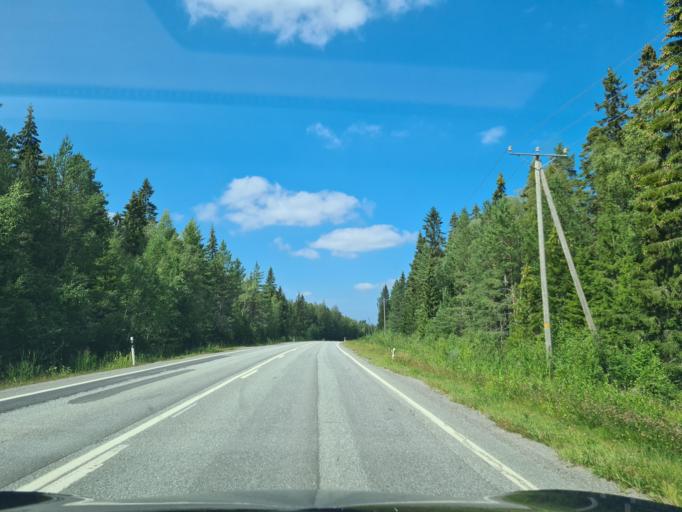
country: FI
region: Ostrobothnia
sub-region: Vaasa
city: Vaasa
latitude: 63.1828
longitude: 21.5697
